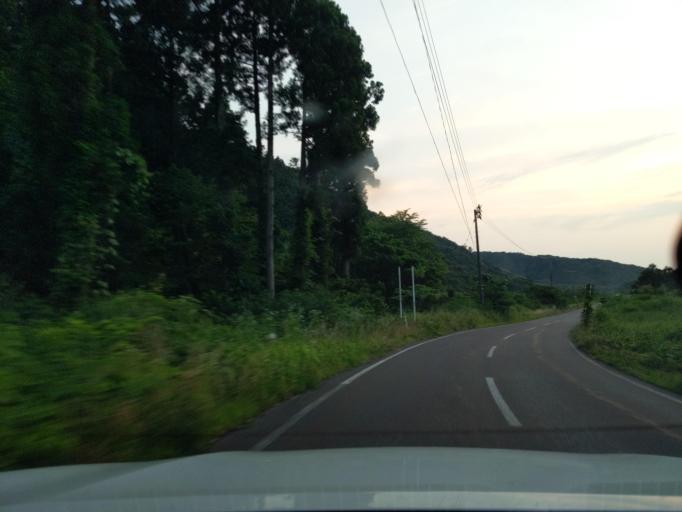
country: JP
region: Niigata
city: Kashiwazaki
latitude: 37.4515
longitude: 138.6251
